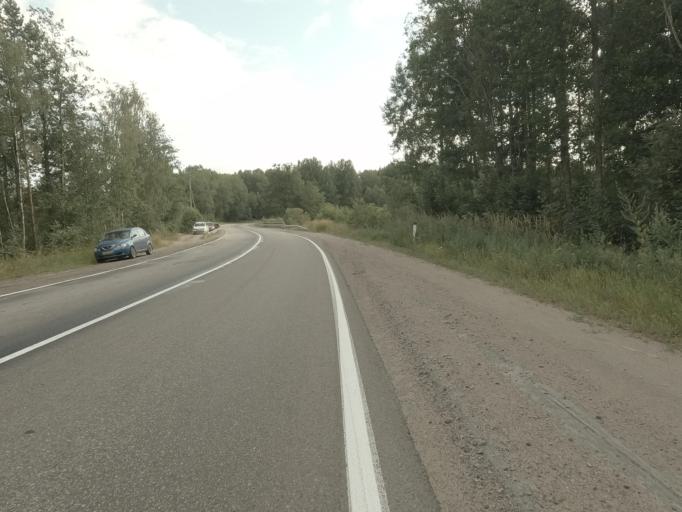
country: RU
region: Leningrad
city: Kamennogorsk
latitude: 60.8689
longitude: 28.9784
